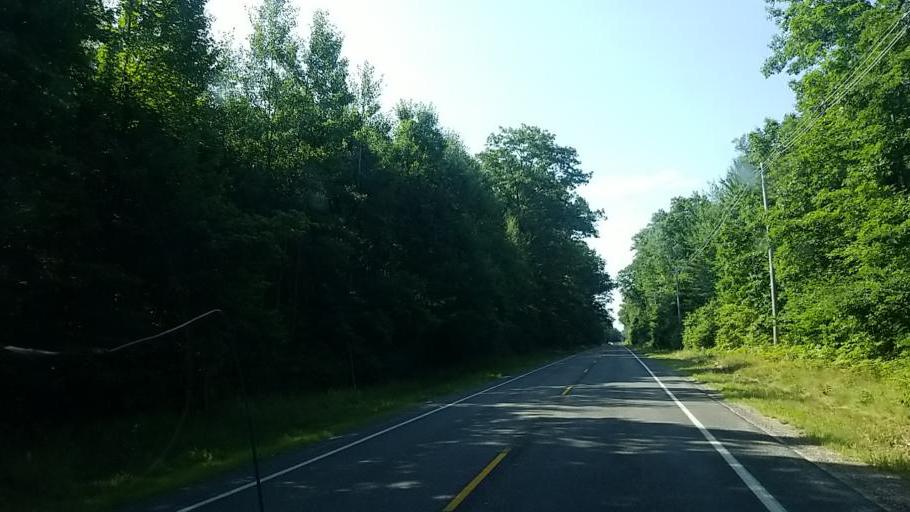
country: US
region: Michigan
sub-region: Muskegon County
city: Whitehall
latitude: 43.3555
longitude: -86.3764
